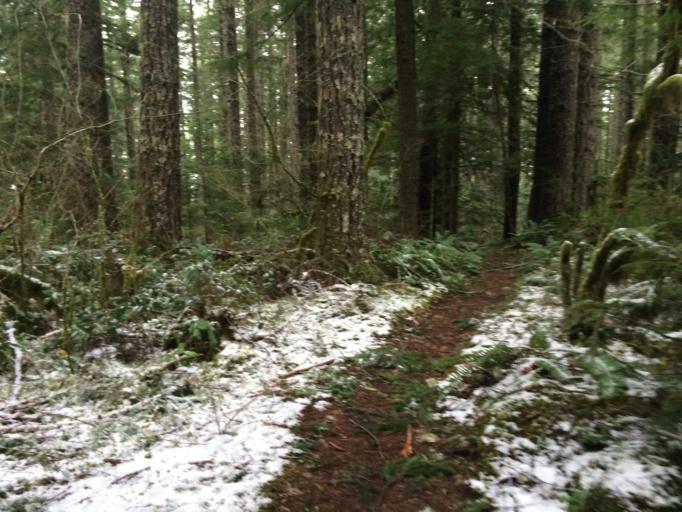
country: US
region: Oregon
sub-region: Benton County
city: Philomath
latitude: 44.5299
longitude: -123.5472
